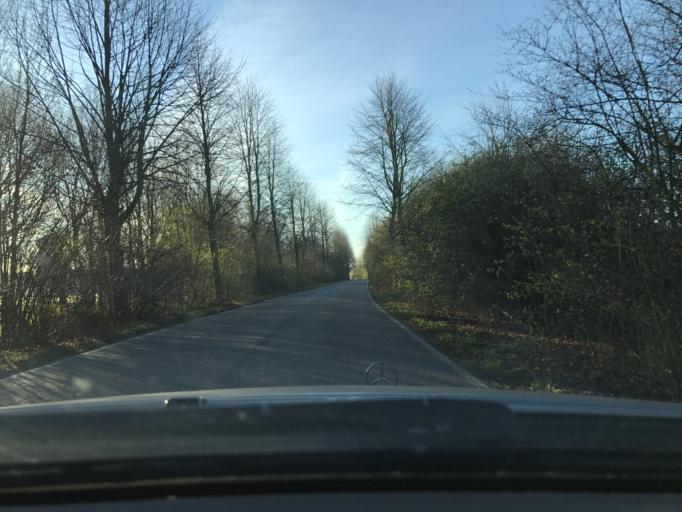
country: DE
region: North Rhine-Westphalia
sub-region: Regierungsbezirk Dusseldorf
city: Krefeld
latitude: 51.3790
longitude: 6.6091
